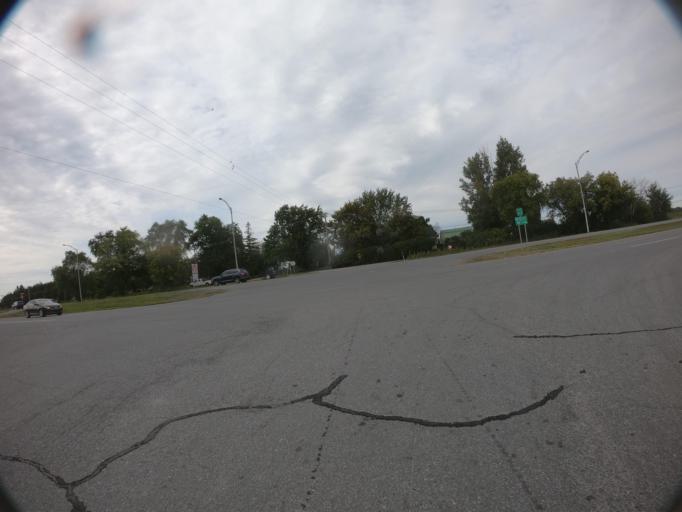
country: CA
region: Quebec
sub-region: Monteregie
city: Richelieu
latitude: 45.4385
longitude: -73.2269
